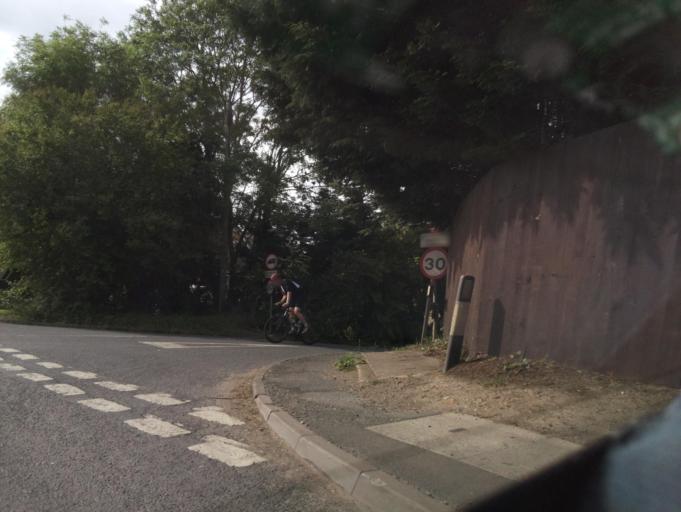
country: GB
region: England
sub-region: Worcestershire
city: Evesham
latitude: 52.0973
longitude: -2.0091
